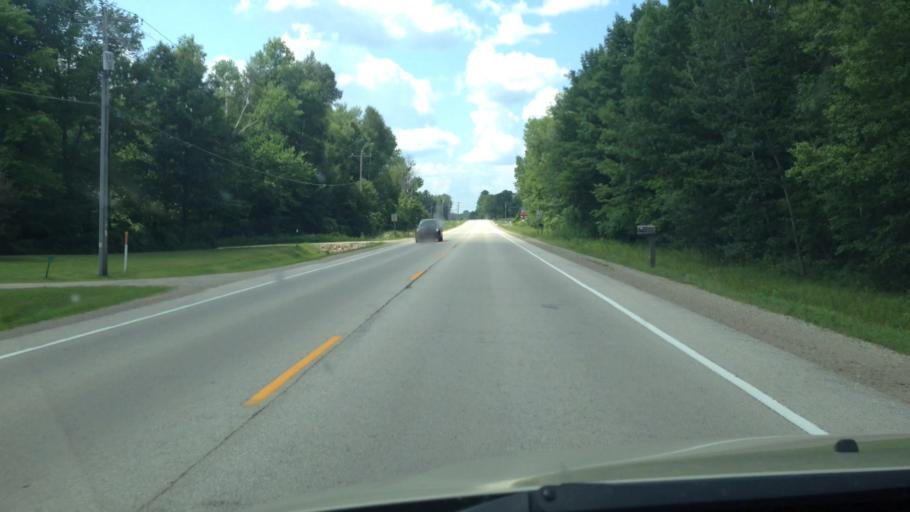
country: US
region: Wisconsin
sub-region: Brown County
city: Suamico
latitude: 44.6410
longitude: -88.0788
